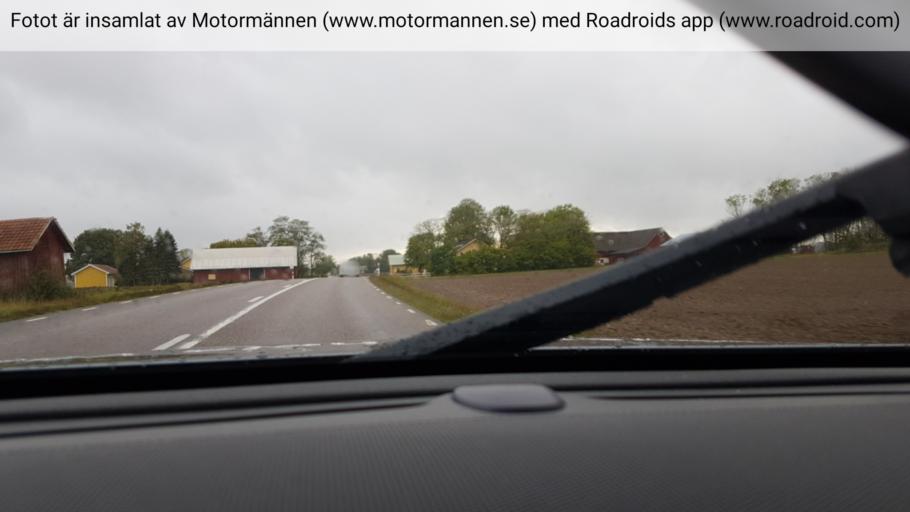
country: SE
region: Vaestra Goetaland
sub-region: Vanersborgs Kommun
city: Bralanda
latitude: 58.5738
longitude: 12.3863
